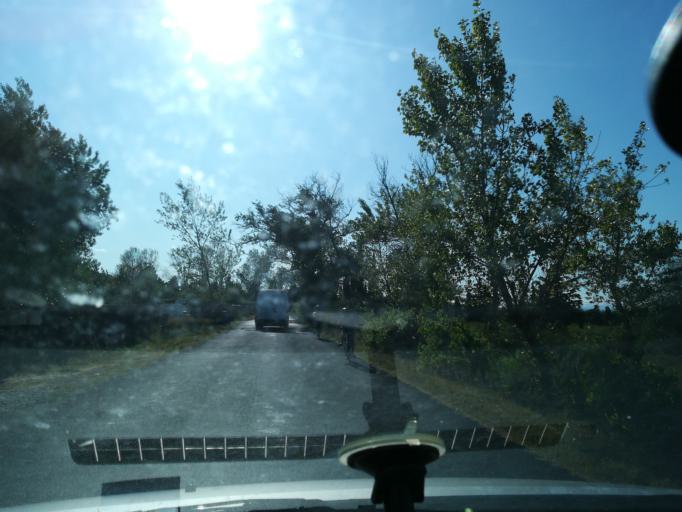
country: FR
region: Languedoc-Roussillon
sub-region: Departement de l'Herault
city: Vias
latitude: 43.2910
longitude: 3.3837
